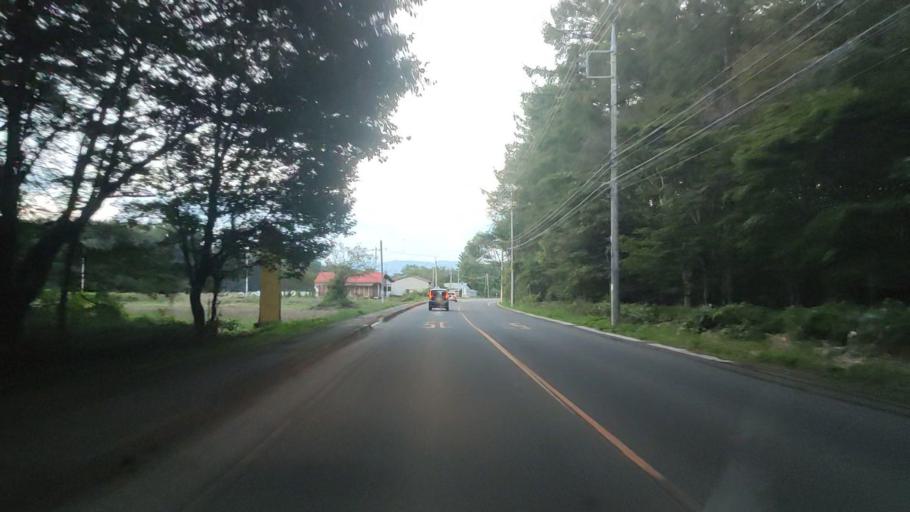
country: JP
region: Nagano
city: Komoro
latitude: 36.5057
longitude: 138.5921
